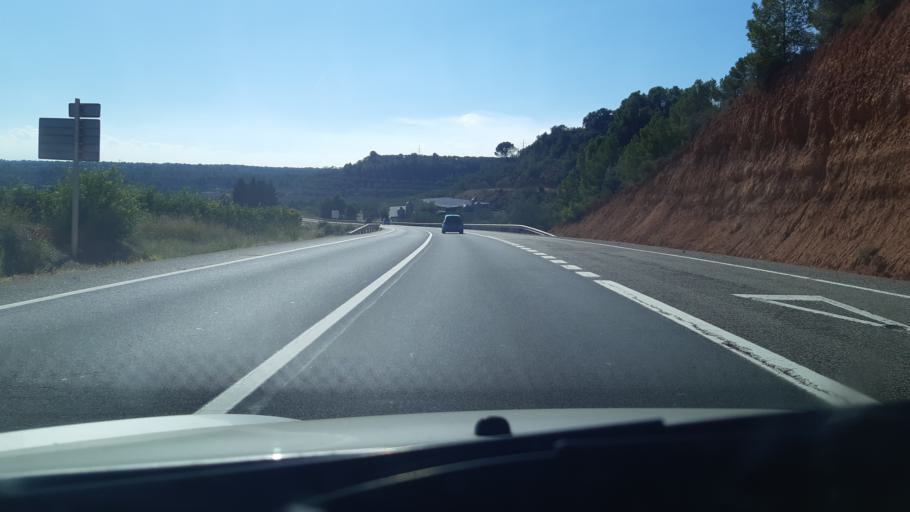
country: ES
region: Catalonia
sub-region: Provincia de Tarragona
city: Tivenys
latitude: 40.9113
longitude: 0.4844
